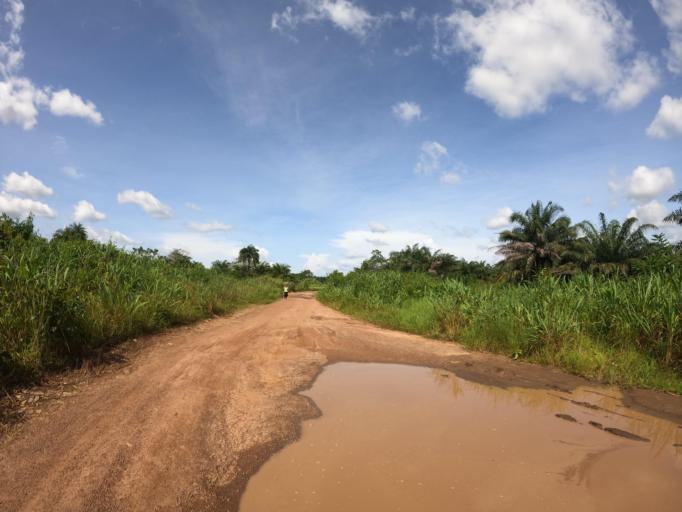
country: SL
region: Northern Province
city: Makeni
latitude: 8.8513
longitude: -12.0284
